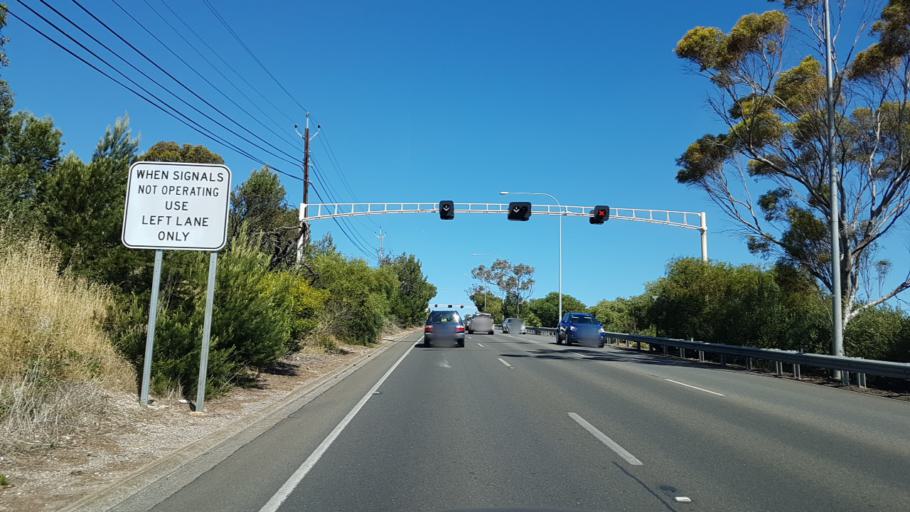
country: AU
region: South Australia
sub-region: Onkaparinga
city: Bedford Park
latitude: -35.0309
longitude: 138.5607
